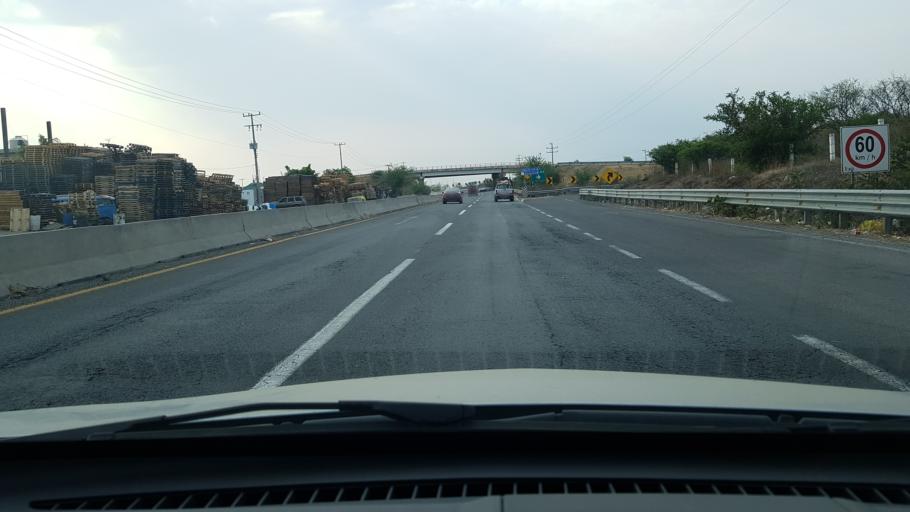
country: MX
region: Morelos
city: Amayuca
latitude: 18.7290
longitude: -98.8101
